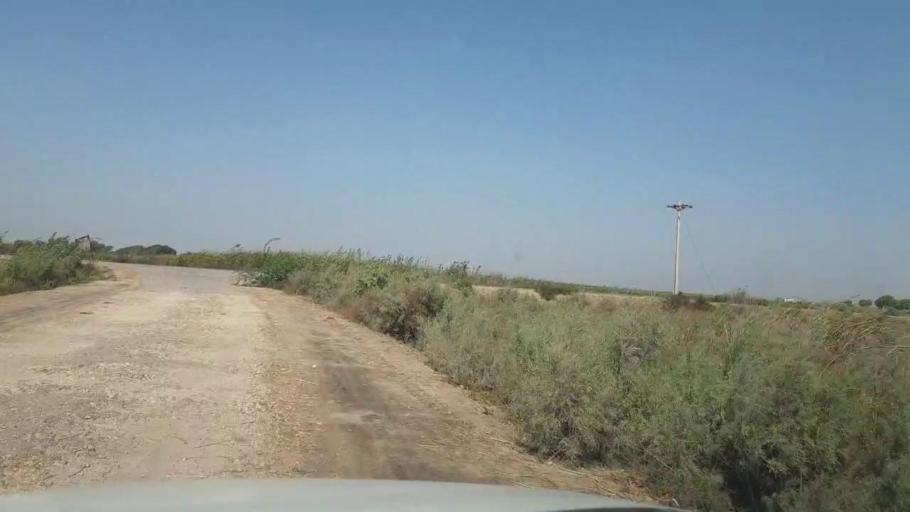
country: PK
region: Sindh
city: Chuhar Jamali
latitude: 24.3826
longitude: 67.8018
